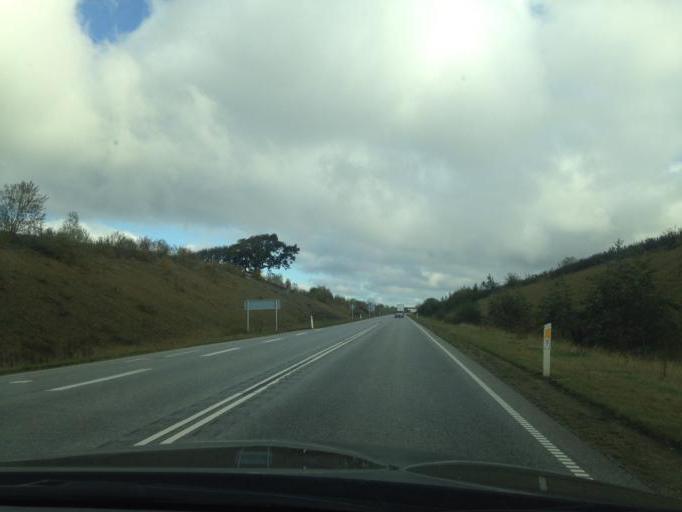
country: DK
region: South Denmark
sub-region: Vejle Kommune
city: Give
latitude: 55.8288
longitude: 9.2567
